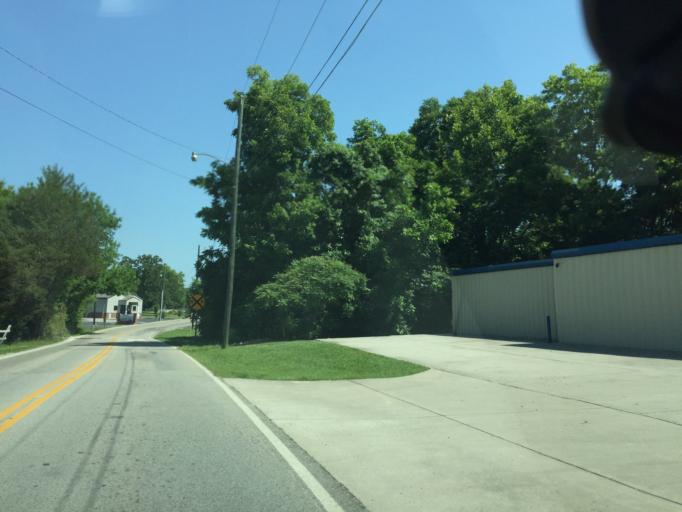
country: US
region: Tennessee
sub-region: Hamilton County
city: Collegedale
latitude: 35.0696
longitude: -85.0641
